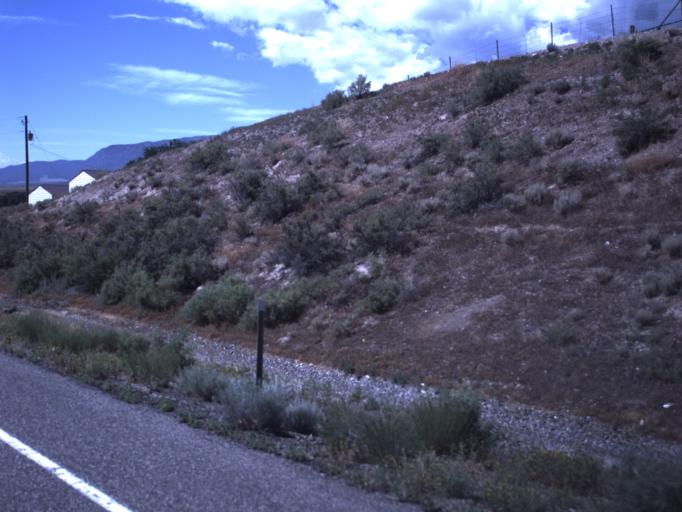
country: US
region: Utah
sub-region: Sevier County
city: Monroe
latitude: 38.4581
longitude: -112.2314
